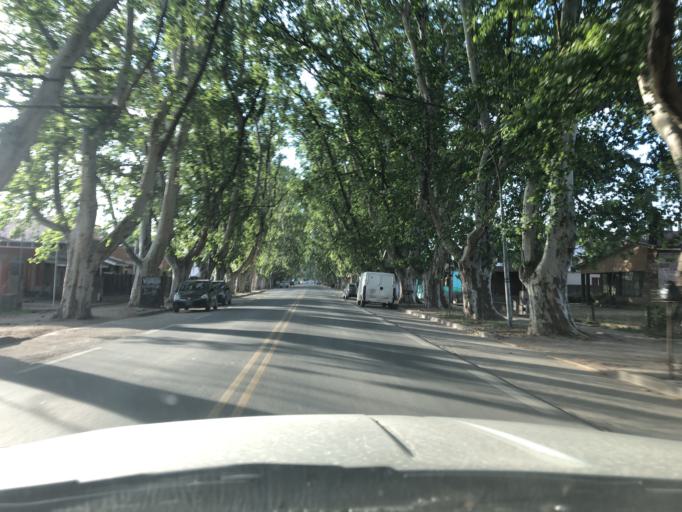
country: AR
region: Cordoba
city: Jesus Maria
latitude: -31.0015
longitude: -64.0849
